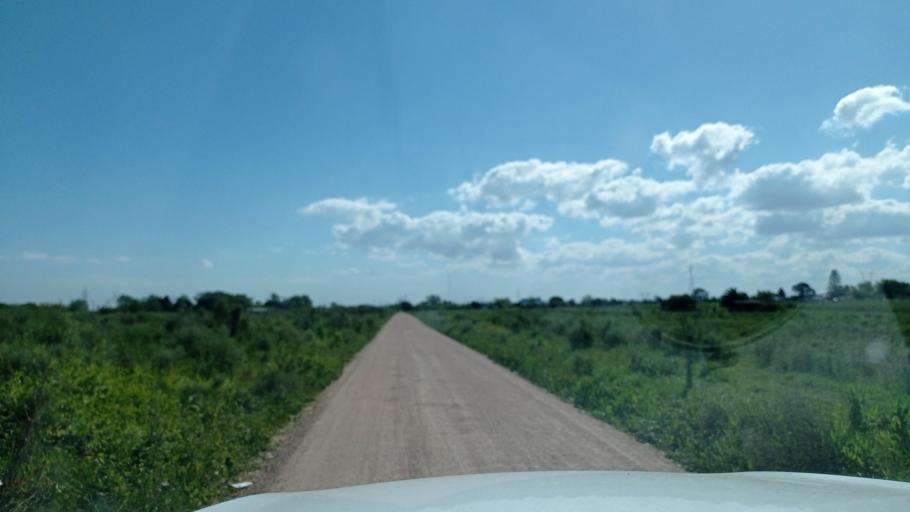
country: UY
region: Canelones
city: La Paz
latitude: -34.7824
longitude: -56.1606
